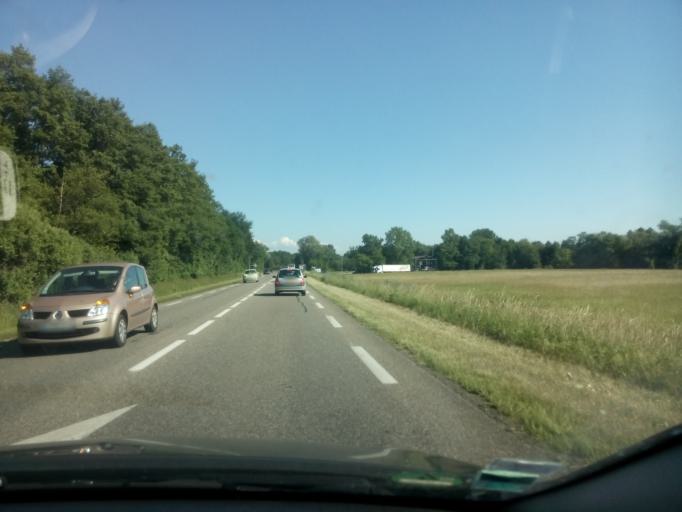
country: FR
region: Alsace
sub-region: Departement du Bas-Rhin
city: Kaltenhouse
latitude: 48.7948
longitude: 7.8415
